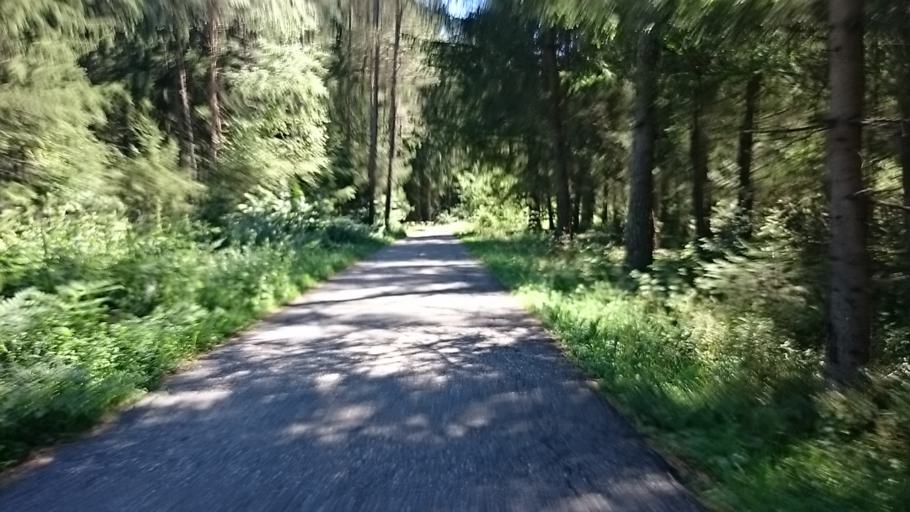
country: IT
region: Trentino-Alto Adige
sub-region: Bolzano
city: Chienes
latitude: 46.7940
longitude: 11.8521
